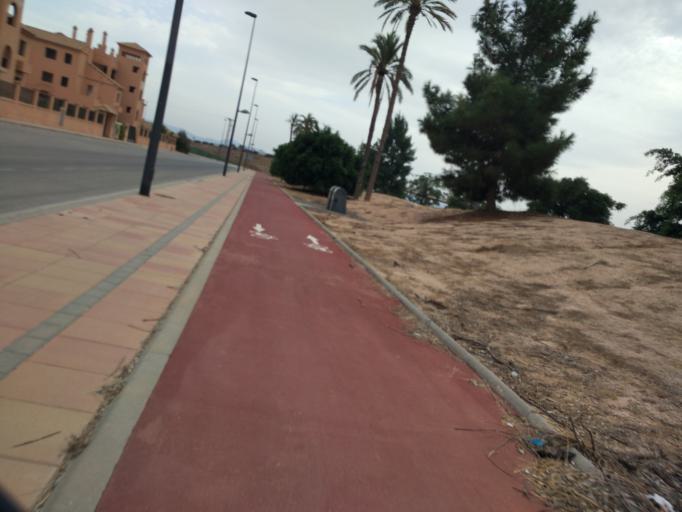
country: ES
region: Murcia
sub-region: Murcia
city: Los Alcazares
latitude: 37.7227
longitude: -0.8699
